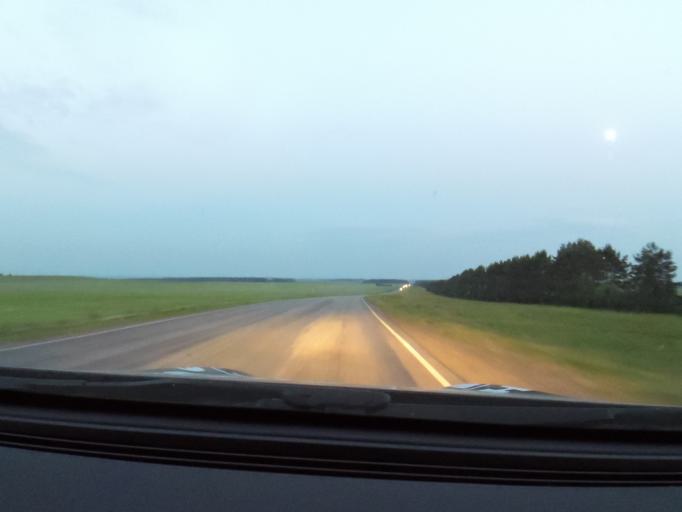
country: RU
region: Bashkortostan
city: Duvan
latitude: 56.1122
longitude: 58.0513
